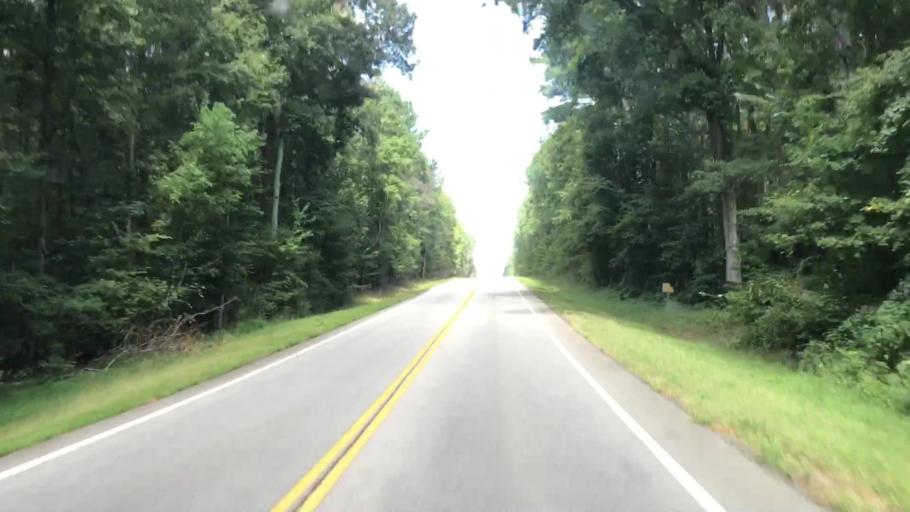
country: US
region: Georgia
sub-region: Greene County
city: Greensboro
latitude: 33.6249
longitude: -83.2136
